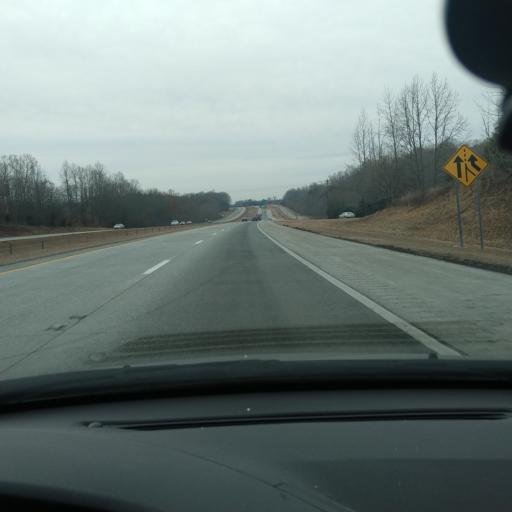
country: US
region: North Carolina
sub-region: Davidson County
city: Lexington
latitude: 35.8127
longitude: -80.2865
